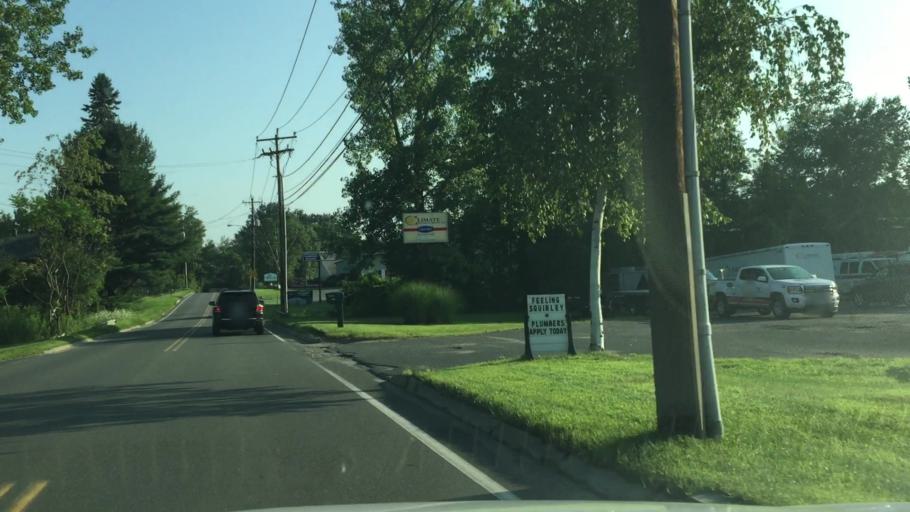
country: US
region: Massachusetts
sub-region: Berkshire County
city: Dalton
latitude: 42.4562
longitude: -73.1900
